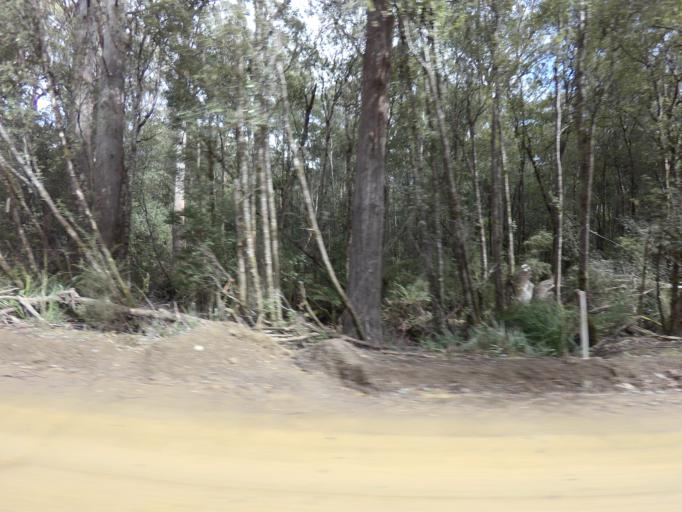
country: AU
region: Tasmania
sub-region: Huon Valley
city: Geeveston
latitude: -43.4097
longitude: 146.8722
